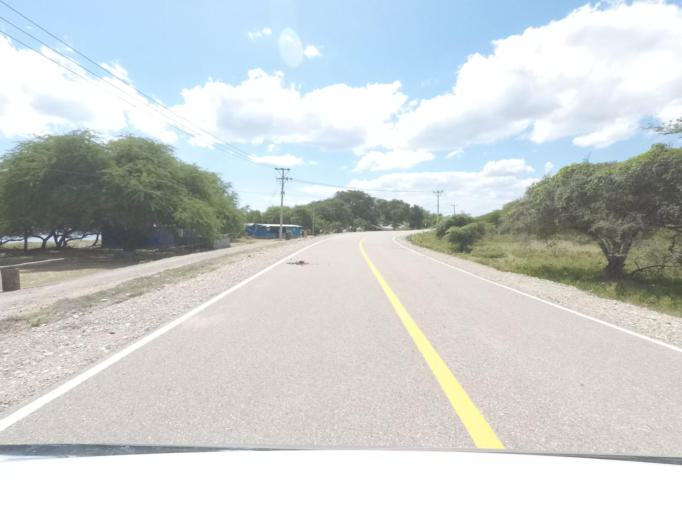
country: TL
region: Baucau
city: Baucau
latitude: -8.4257
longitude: 126.6960
